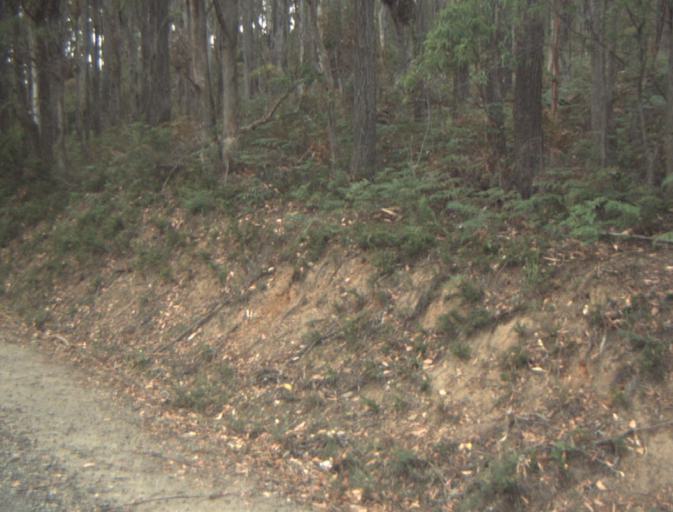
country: AU
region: Tasmania
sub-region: Dorset
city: Scottsdale
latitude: -41.4115
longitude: 147.5175
